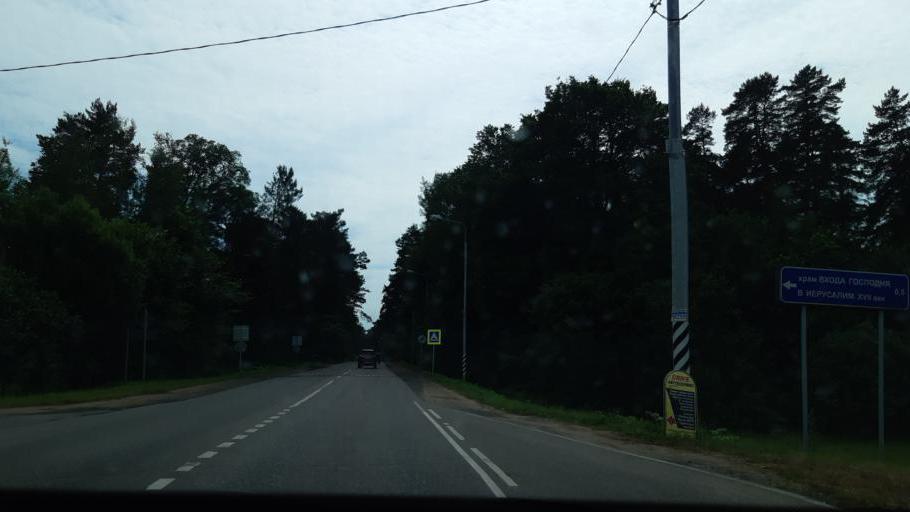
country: RU
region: Moskovskaya
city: Vereya
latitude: 55.3581
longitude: 36.2044
